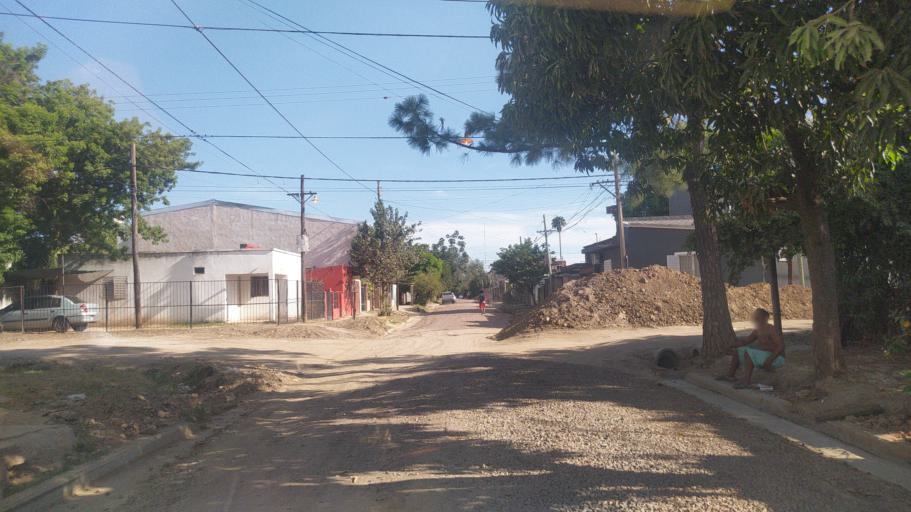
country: AR
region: Corrientes
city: Corrientes
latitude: -27.4889
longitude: -58.8152
